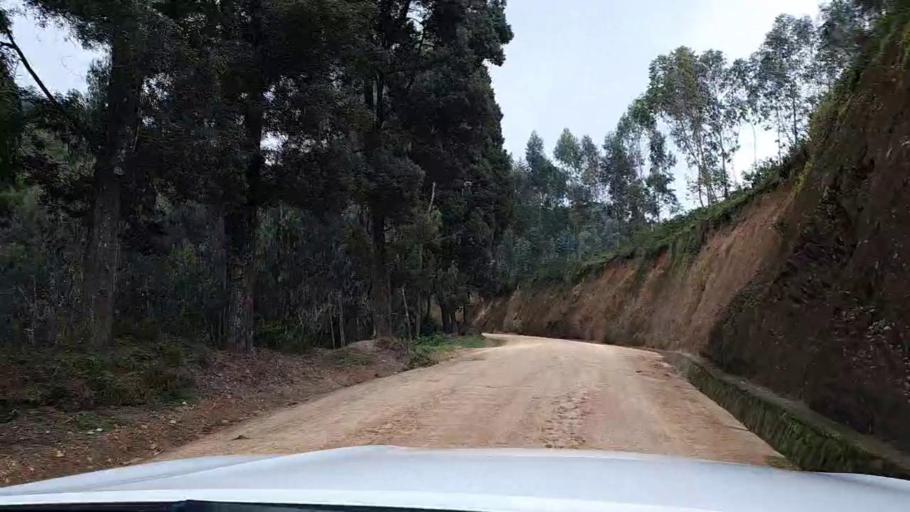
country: RW
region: Southern Province
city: Nzega
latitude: -2.3828
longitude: 29.3840
